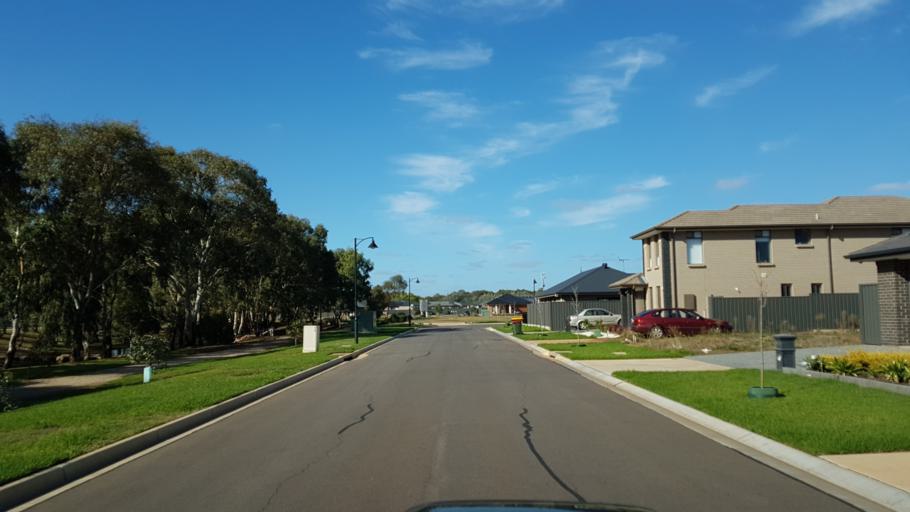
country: AU
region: South Australia
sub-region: Salisbury
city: Salisbury
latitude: -34.7674
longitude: 138.5975
